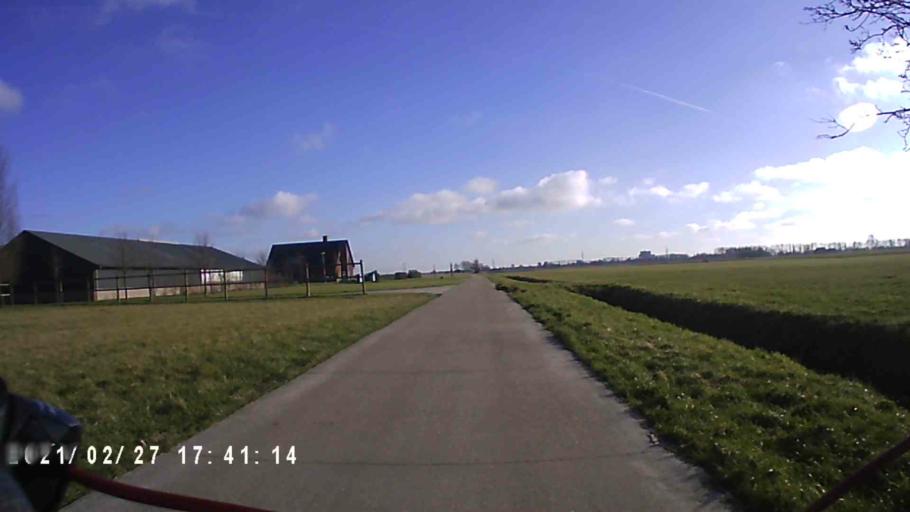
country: NL
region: Groningen
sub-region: Gemeente Bedum
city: Bedum
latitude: 53.3283
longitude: 6.5979
